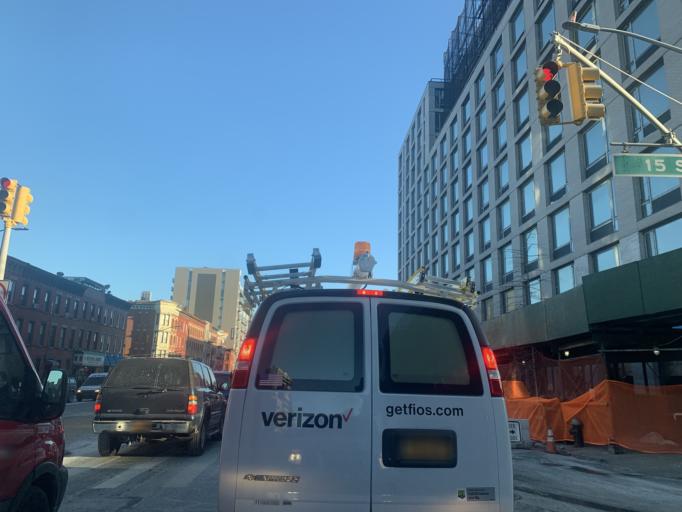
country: US
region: New York
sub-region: Kings County
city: Brooklyn
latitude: 40.6667
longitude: -73.9916
